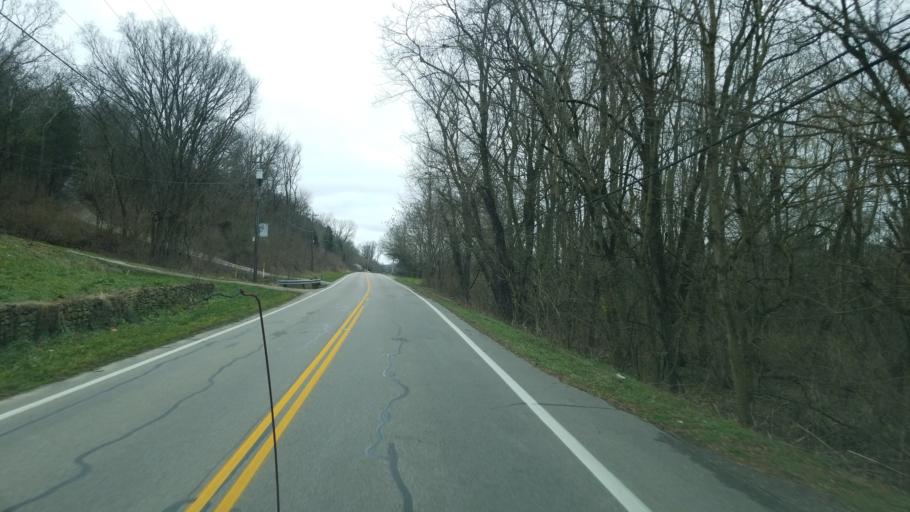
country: US
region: Ohio
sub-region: Clermont County
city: New Richmond
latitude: 38.8500
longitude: -84.2239
